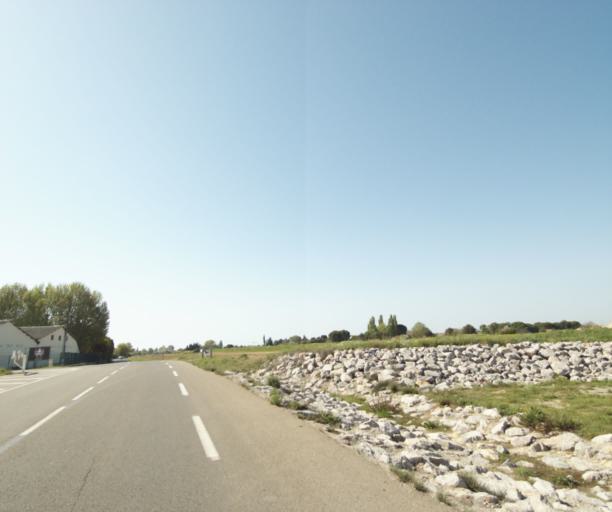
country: FR
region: Languedoc-Roussillon
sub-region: Departement de l'Herault
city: Lattes
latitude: 43.5867
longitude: 3.9082
